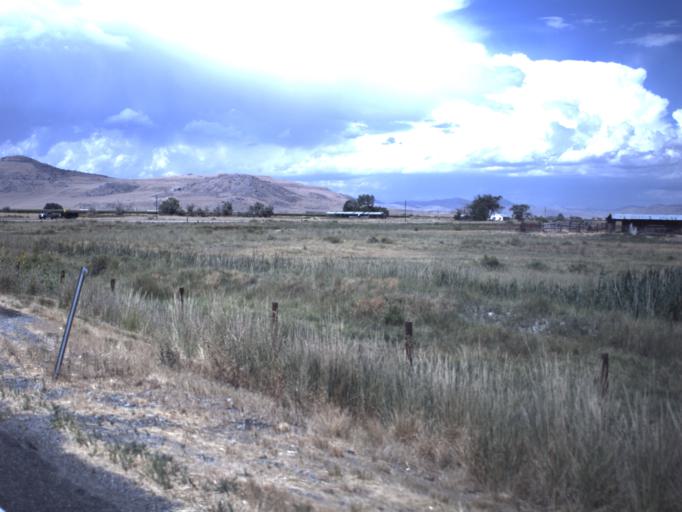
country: US
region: Utah
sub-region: Box Elder County
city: Honeyville
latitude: 41.5648
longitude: -112.1756
